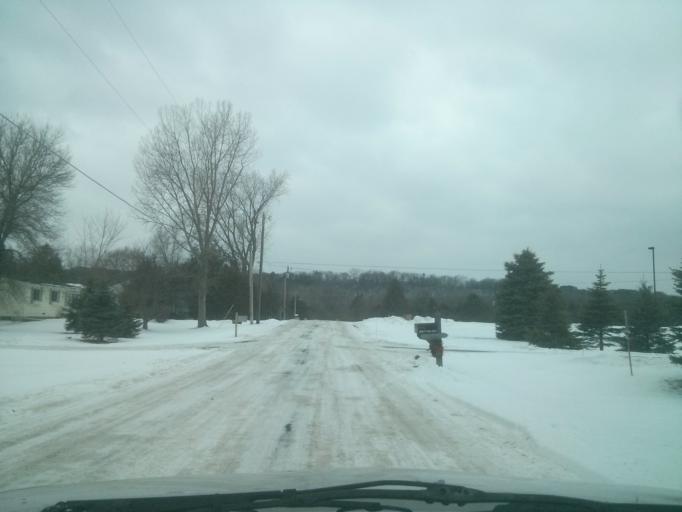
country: US
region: Minnesota
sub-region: Washington County
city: Lake Saint Croix Beach
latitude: 44.9386
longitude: -92.7686
